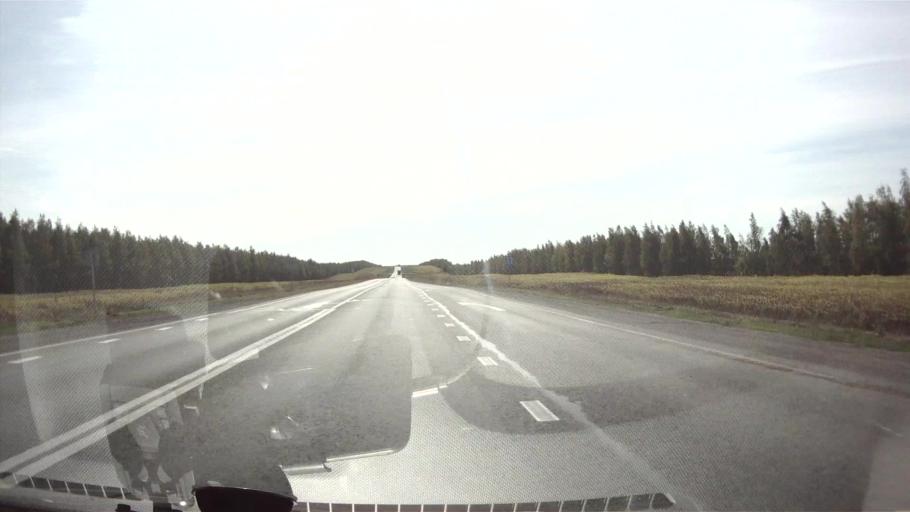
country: RU
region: Samara
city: Syzran'
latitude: 52.9208
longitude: 48.3025
